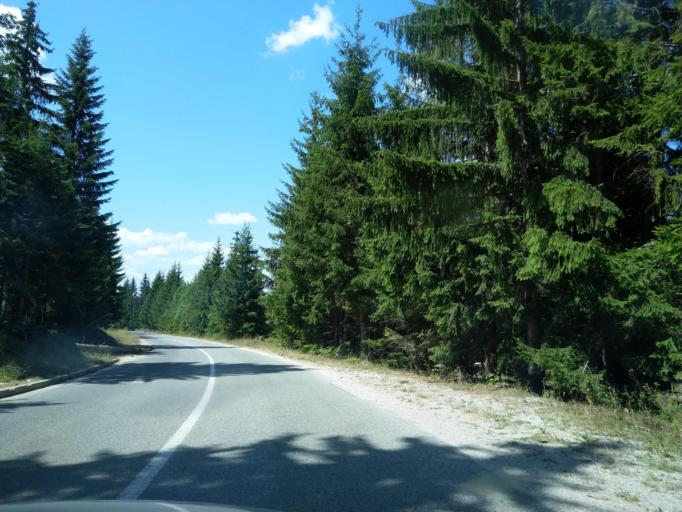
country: RS
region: Central Serbia
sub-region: Zlatiborski Okrug
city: Nova Varos
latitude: 43.4137
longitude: 19.8360
